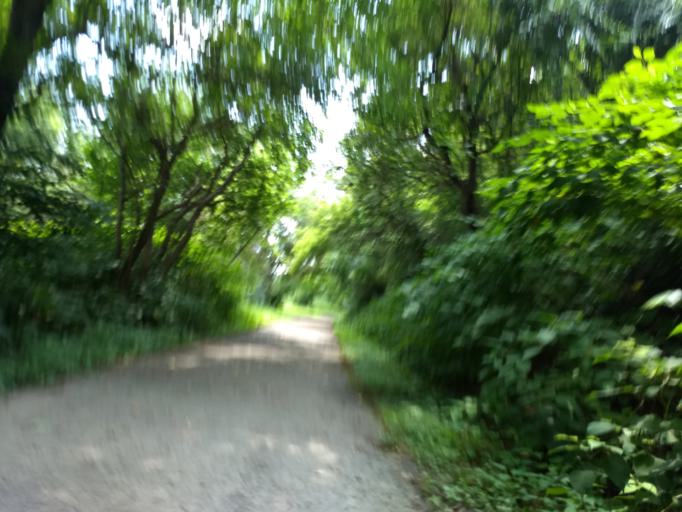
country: US
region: Pennsylvania
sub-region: Allegheny County
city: Homestead
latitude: 40.4082
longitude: -79.9230
